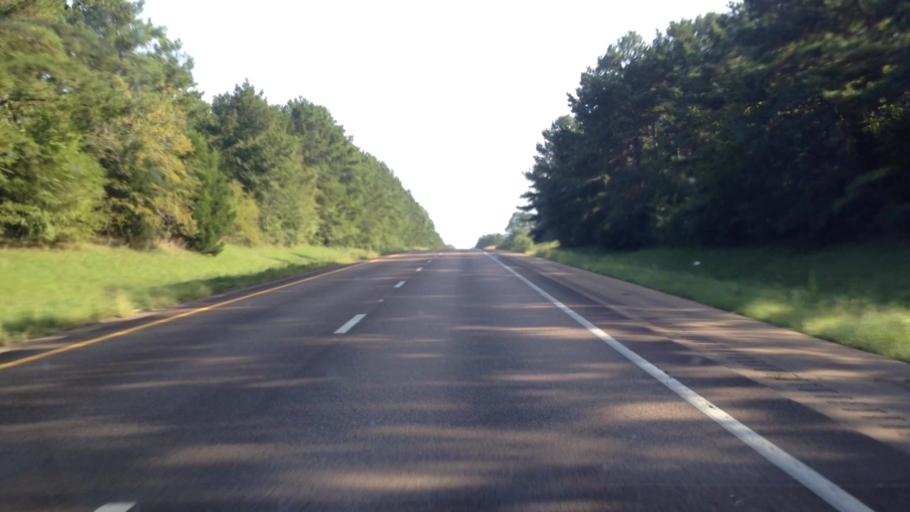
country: US
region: Mississippi
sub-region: Pike County
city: Summit
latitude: 31.3840
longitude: -90.4792
